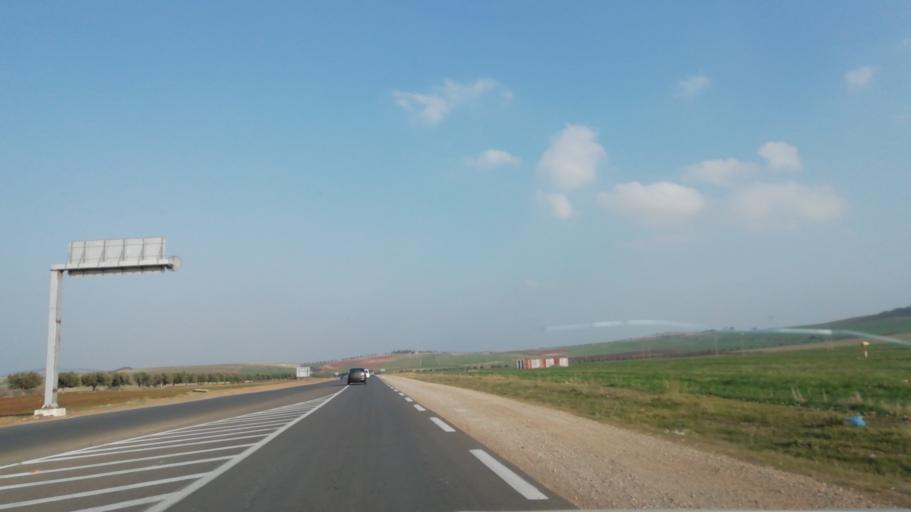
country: DZ
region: Ain Temouchent
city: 'Ain Temouchent
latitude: 35.2952
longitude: -1.0950
